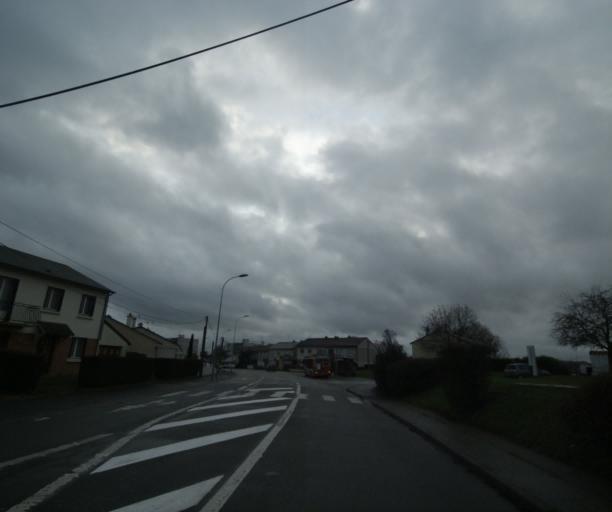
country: FR
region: Pays de la Loire
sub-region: Departement de la Sarthe
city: Coulaines
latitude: 48.0275
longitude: 0.1829
